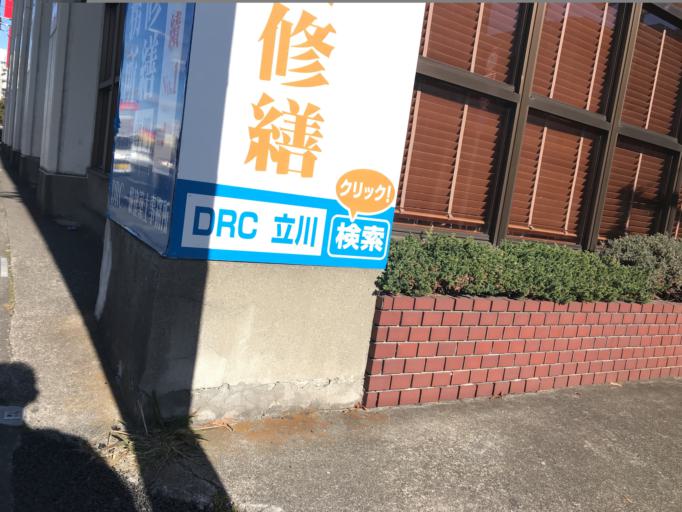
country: JP
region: Tokyo
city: Hino
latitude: 35.7120
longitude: 139.4220
